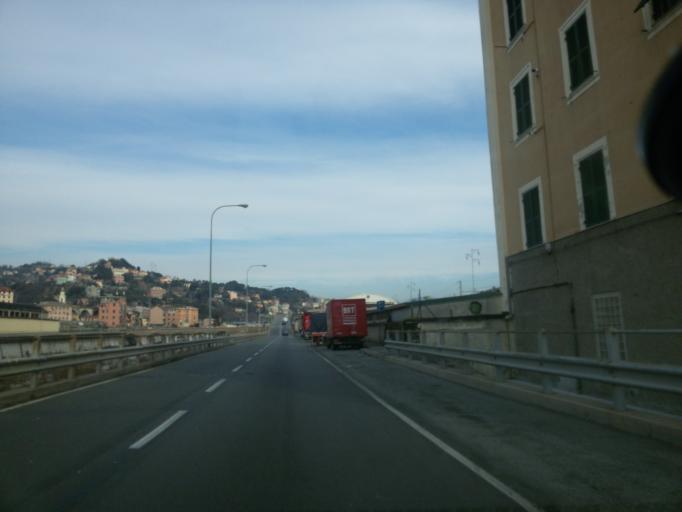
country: IT
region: Liguria
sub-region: Provincia di Genova
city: Genoa
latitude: 44.4477
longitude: 8.8911
